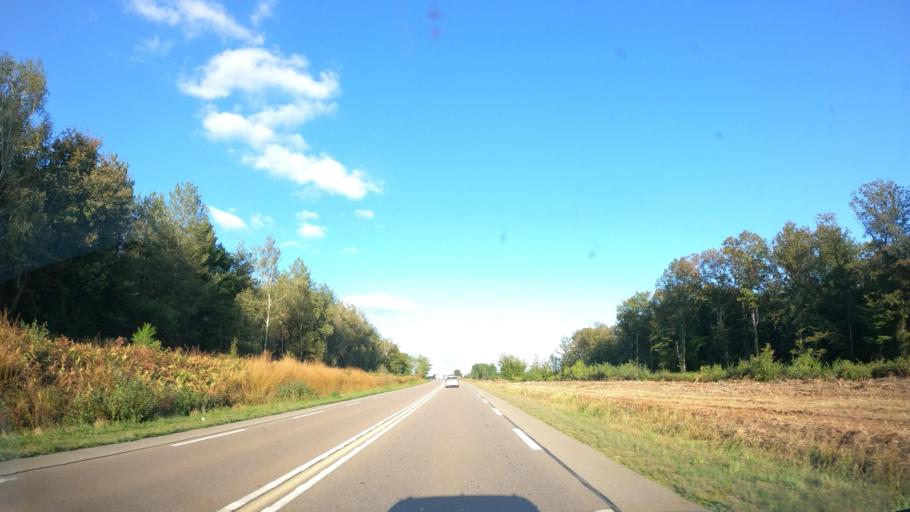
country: FR
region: Bourgogne
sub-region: Departement de Saone-et-Loire
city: Ciry-le-Noble
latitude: 46.6098
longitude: 4.2635
